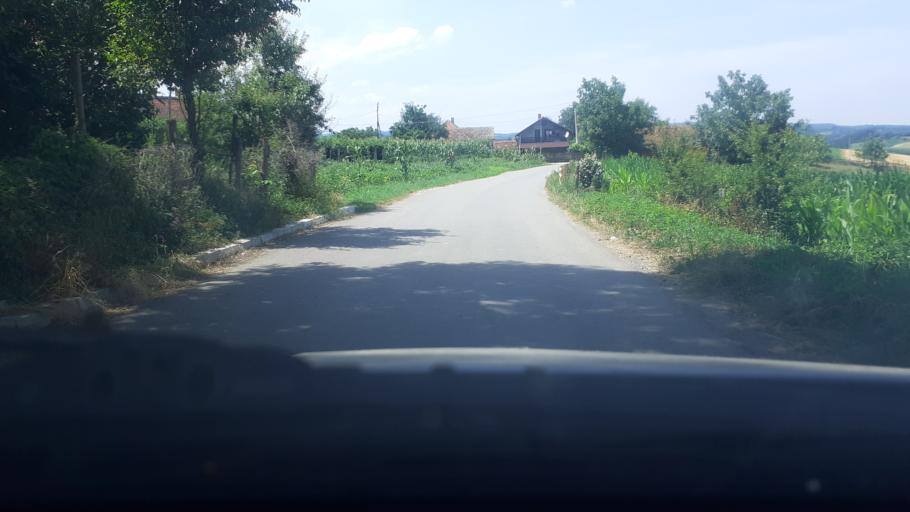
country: RS
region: Central Serbia
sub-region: Kolubarski Okrug
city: Osecina
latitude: 44.3918
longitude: 19.4960
